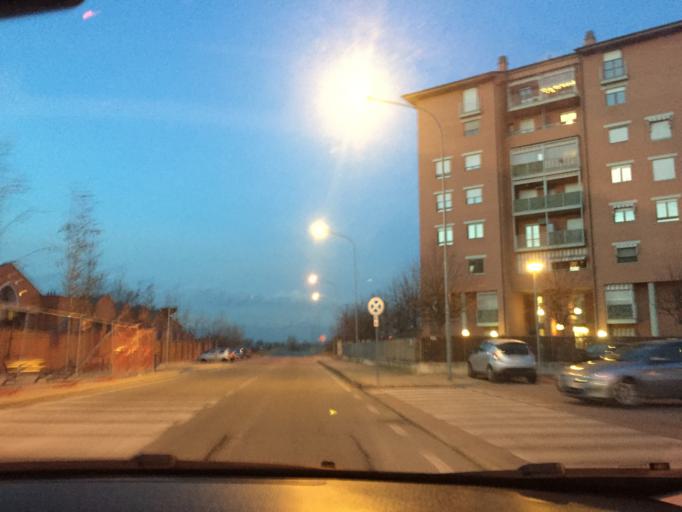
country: IT
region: Piedmont
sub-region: Provincia di Torino
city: Collegno
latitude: 45.0793
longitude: 7.6056
